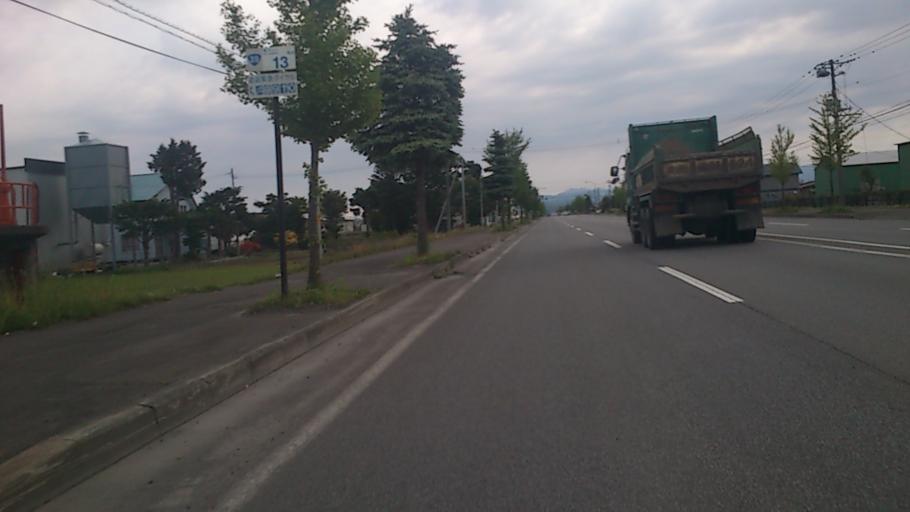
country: JP
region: Hokkaido
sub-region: Asahikawa-shi
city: Asahikawa
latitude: 43.8368
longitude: 142.4759
